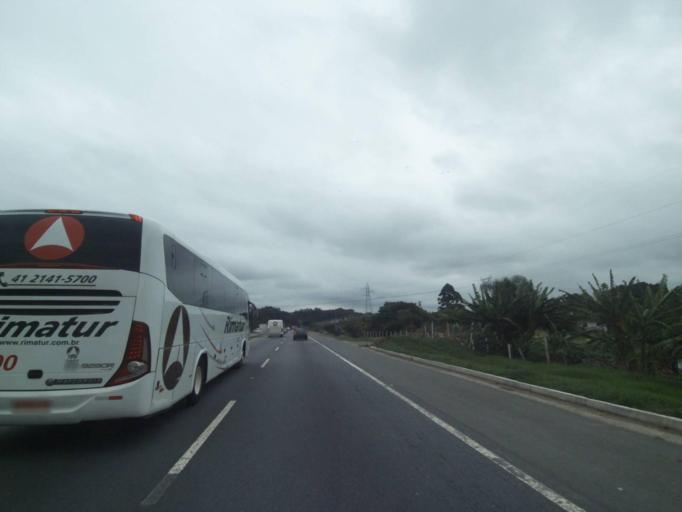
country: BR
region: Parana
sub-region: Araucaria
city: Araucaria
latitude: -25.5545
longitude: -49.3393
